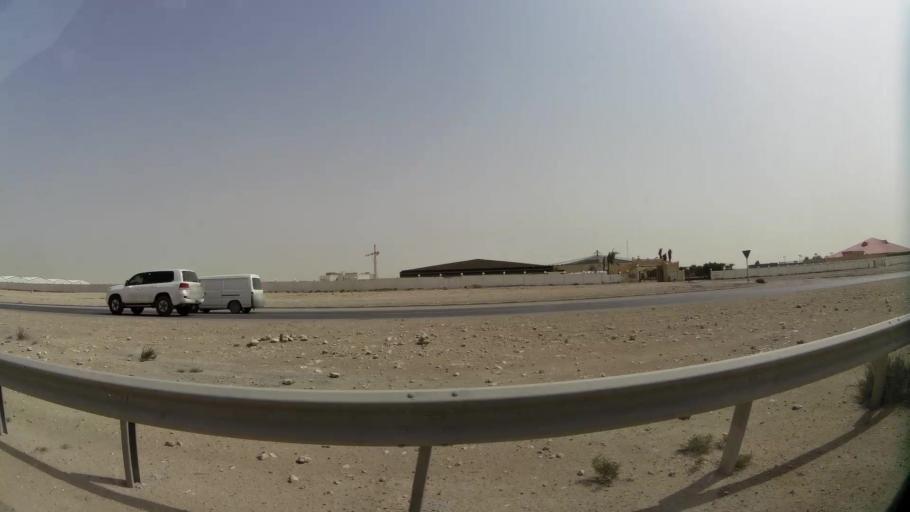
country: QA
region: Baladiyat ar Rayyan
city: Ar Rayyan
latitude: 25.2205
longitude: 51.3624
